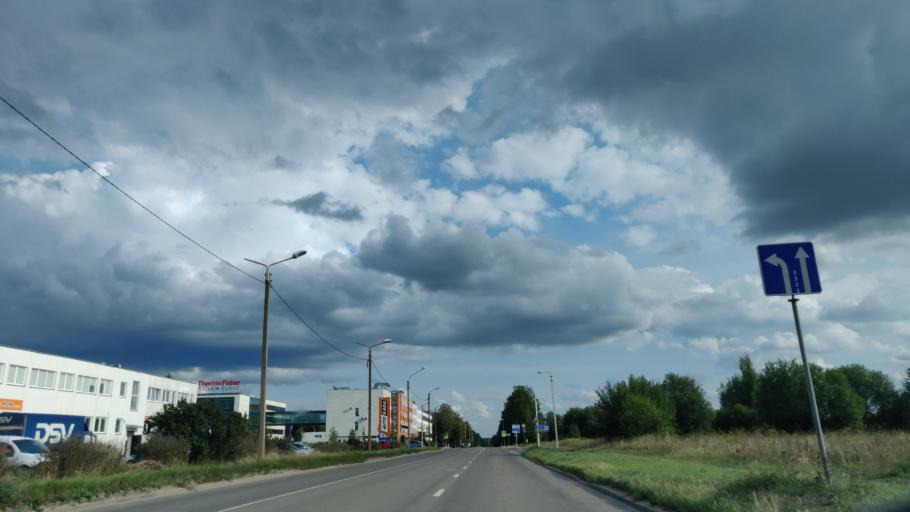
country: LT
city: Baltoji Voke
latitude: 54.6264
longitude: 25.1394
